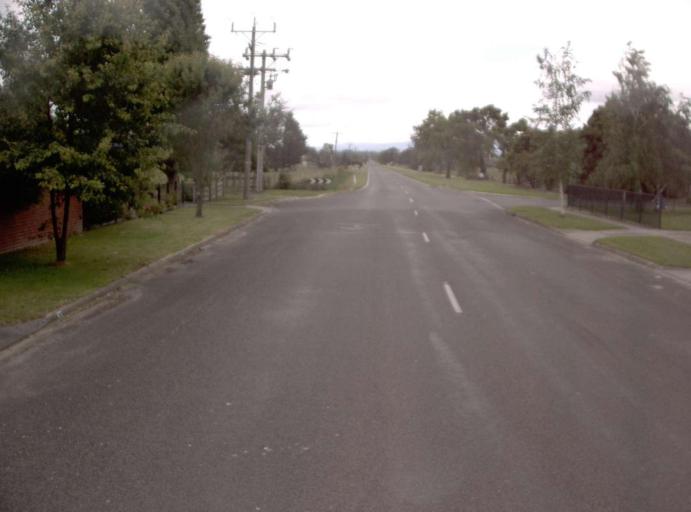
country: AU
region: Victoria
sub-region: Latrobe
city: Moe
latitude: -38.2028
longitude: 146.1522
